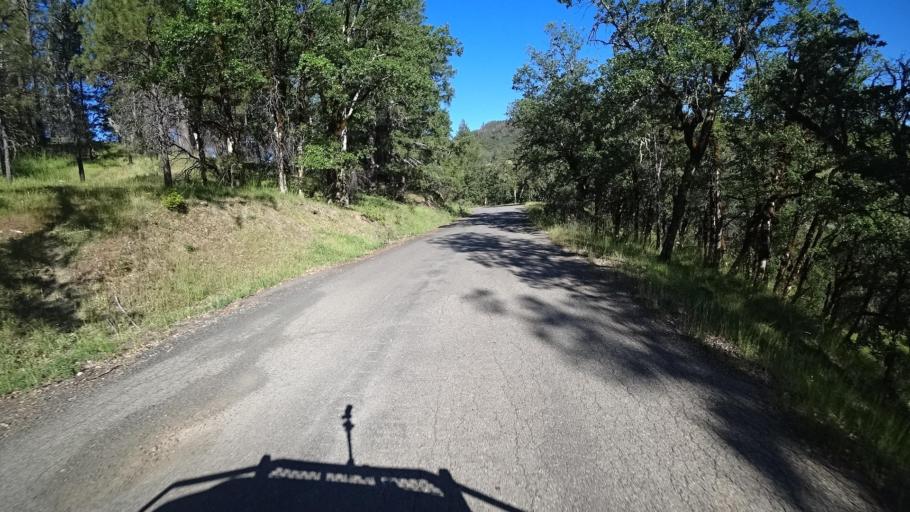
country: US
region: California
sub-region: Lake County
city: Upper Lake
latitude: 39.4087
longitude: -122.9787
